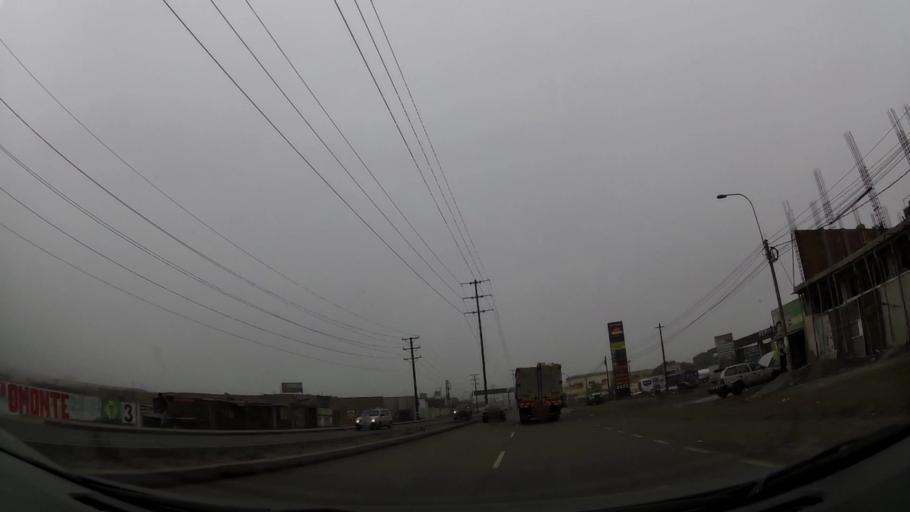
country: PE
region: Lima
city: Ventanilla
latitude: -11.8415
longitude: -77.1143
